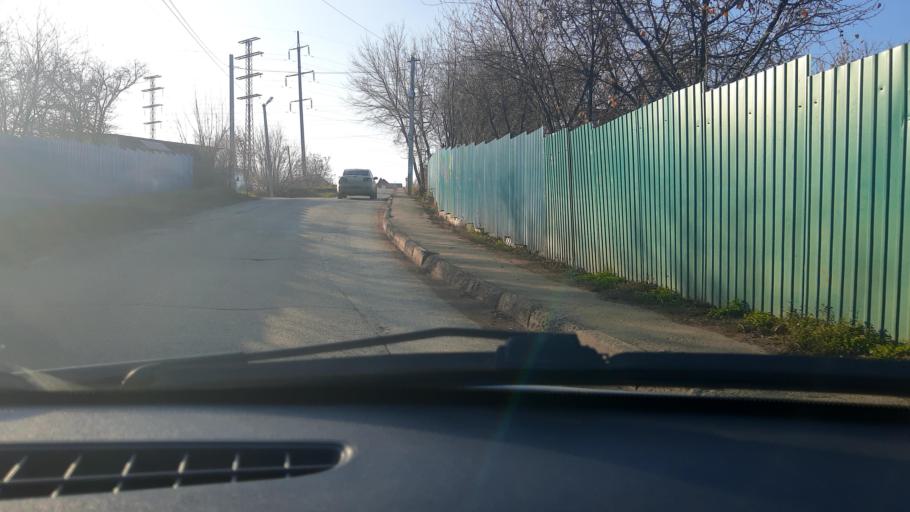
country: RU
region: Bashkortostan
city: Avdon
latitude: 54.6957
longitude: 55.8124
